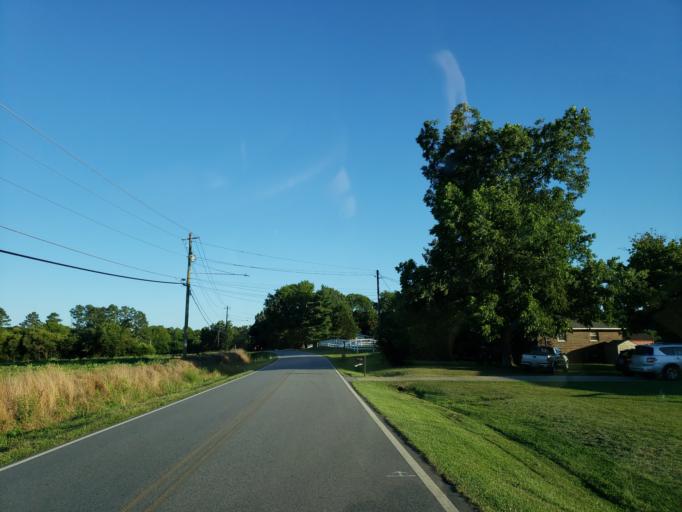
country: US
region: Georgia
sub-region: Bartow County
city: Euharlee
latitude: 34.0911
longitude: -84.9907
